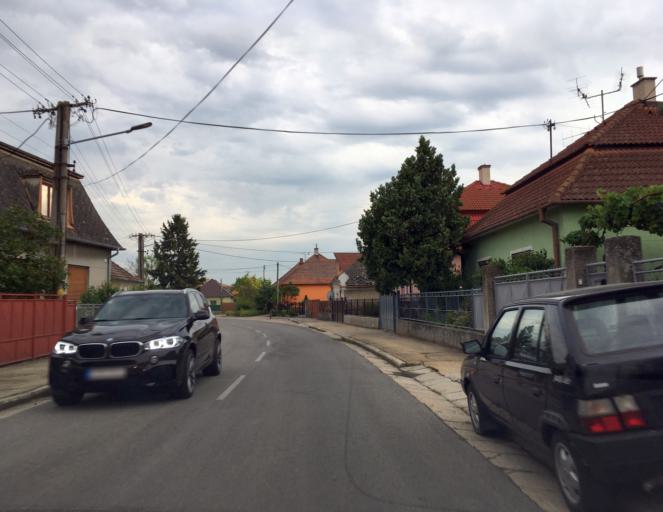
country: SK
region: Trnavsky
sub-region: Okres Dunajska Streda
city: Velky Meder
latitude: 47.9176
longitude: 17.6912
